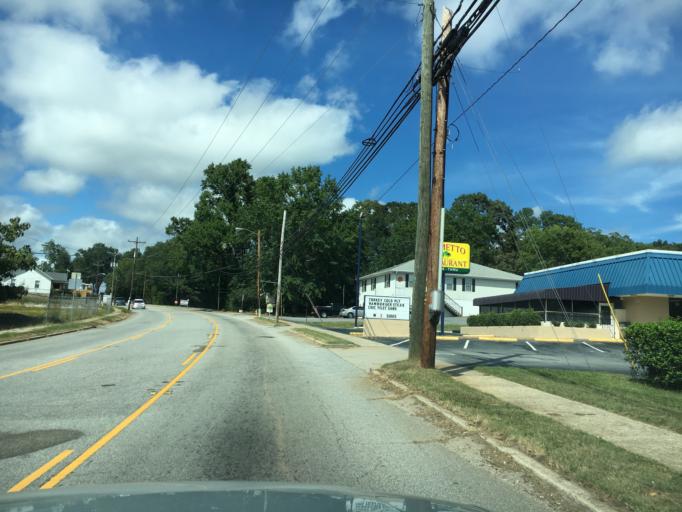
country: US
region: South Carolina
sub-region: Spartanburg County
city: Inman
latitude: 35.0429
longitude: -82.0893
